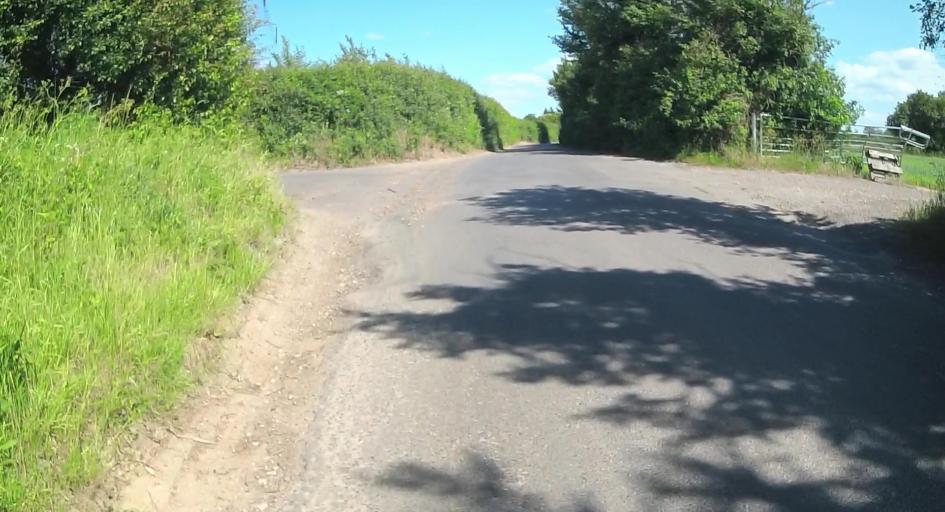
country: GB
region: England
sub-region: Hampshire
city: Hook
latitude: 51.3125
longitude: -0.9911
